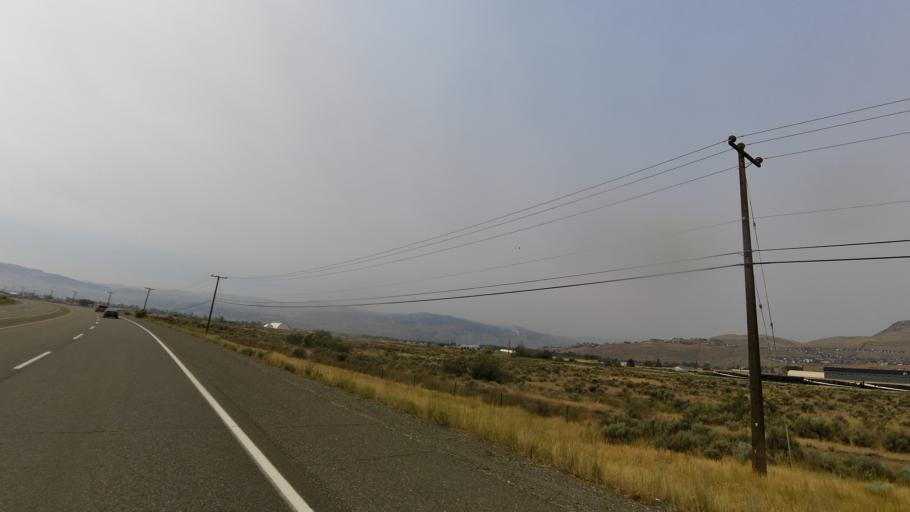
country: CA
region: British Columbia
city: Kamloops
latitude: 50.7303
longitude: -120.3378
